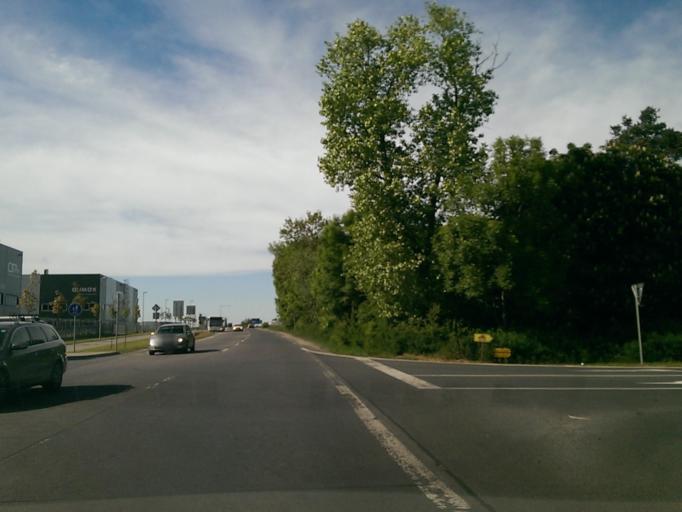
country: CZ
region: Praha
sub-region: Praha 20
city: Horni Pocernice
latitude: 50.1222
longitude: 14.6247
